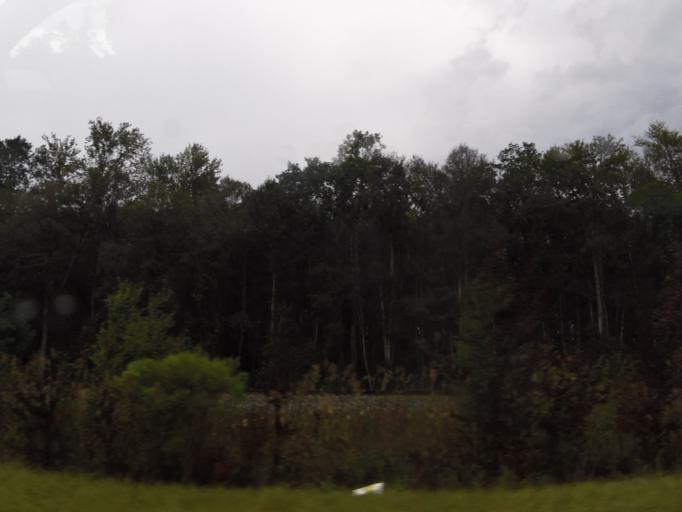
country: US
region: Georgia
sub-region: Wayne County
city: Jesup
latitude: 31.4870
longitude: -81.7395
